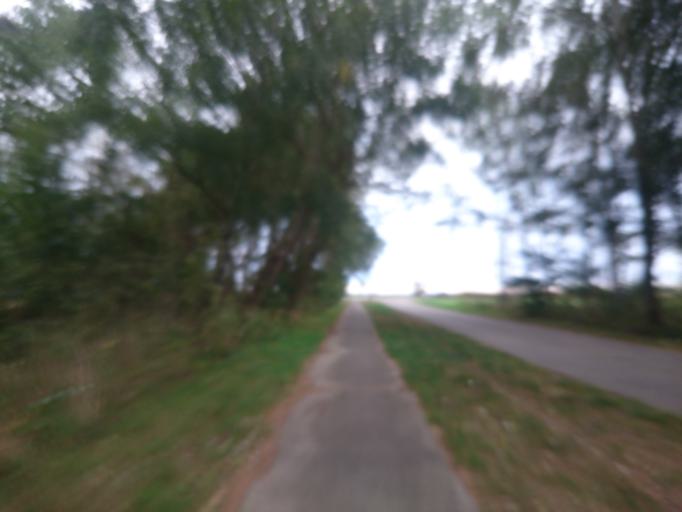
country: DE
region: Mecklenburg-Vorpommern
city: Zingst
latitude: 54.3758
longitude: 12.6525
